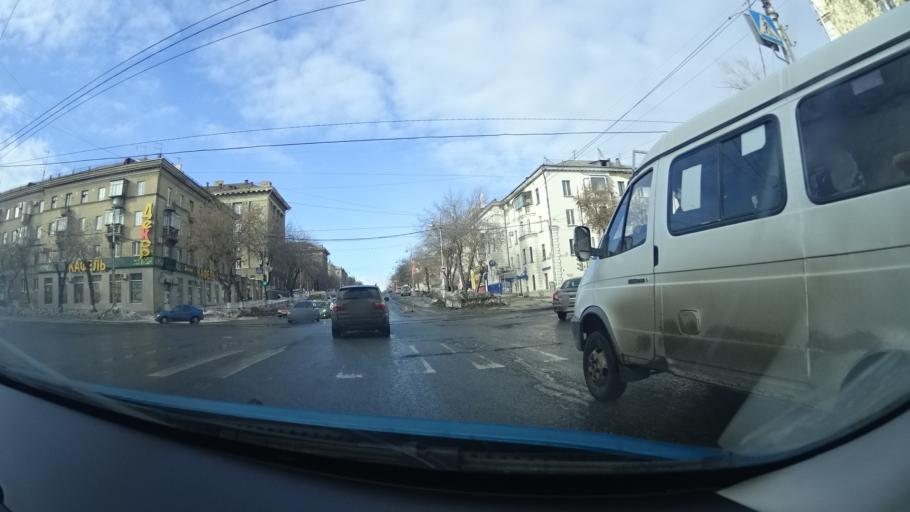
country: RU
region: Chelyabinsk
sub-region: Gorod Magnitogorsk
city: Magnitogorsk
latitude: 53.4258
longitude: 58.9837
